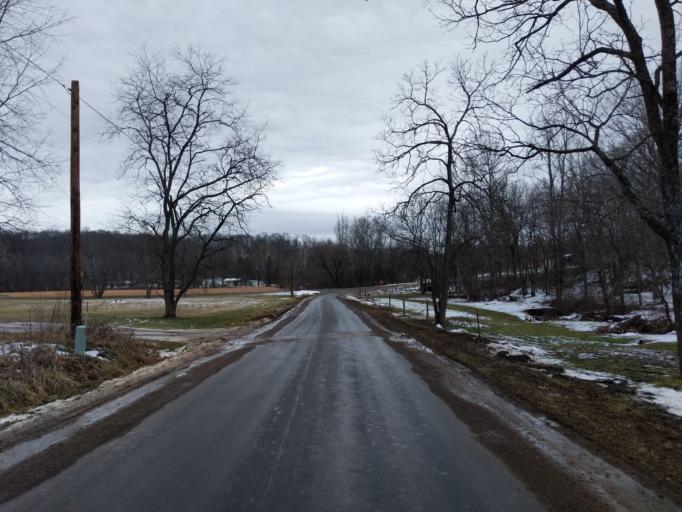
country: US
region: Ohio
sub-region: Athens County
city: The Plains
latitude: 39.3372
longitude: -82.1838
